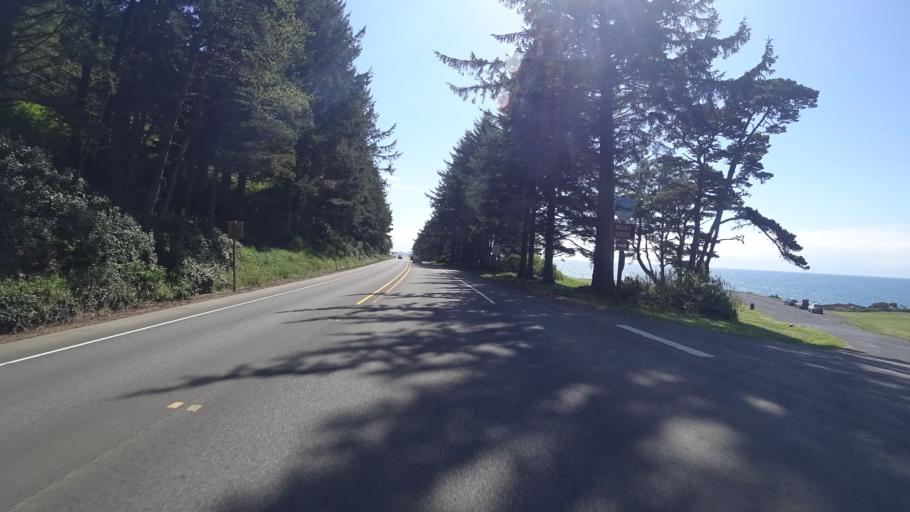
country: US
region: Oregon
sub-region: Lincoln County
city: Depoe Bay
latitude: 44.7853
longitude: -124.0716
